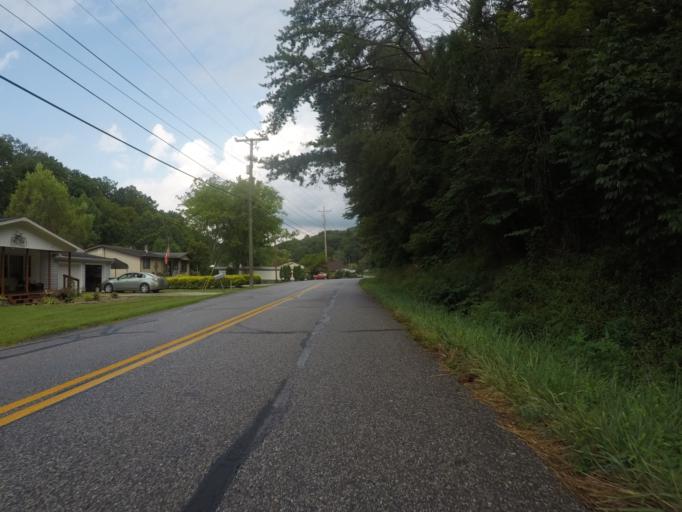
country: US
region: Kentucky
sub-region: Boyd County
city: Meads
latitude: 38.4156
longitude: -82.6890
